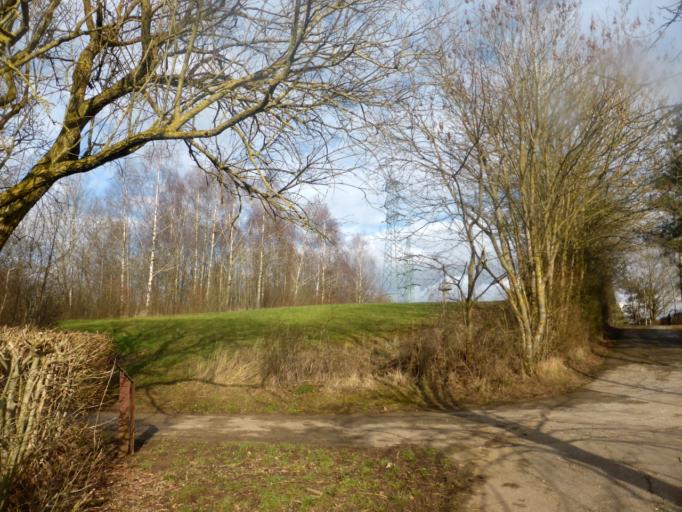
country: LU
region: Luxembourg
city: Belvaux
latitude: 49.5150
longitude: 5.9298
